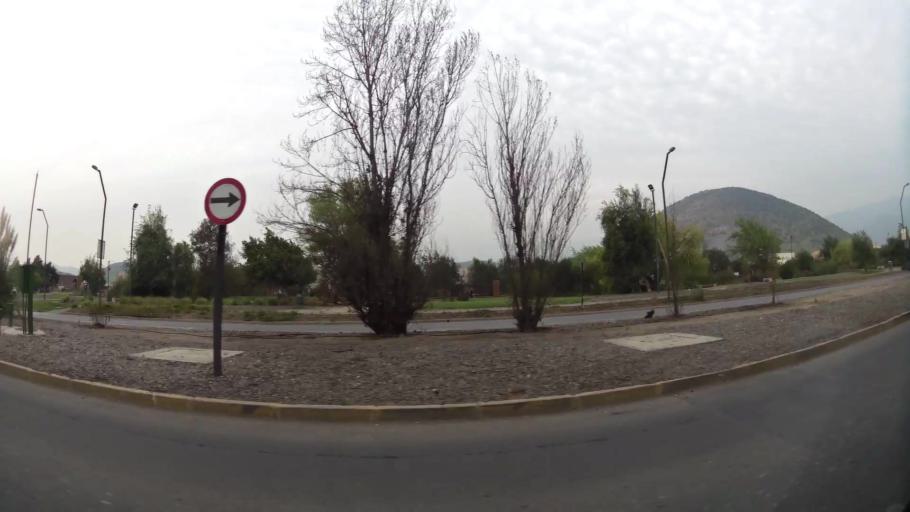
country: CL
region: Santiago Metropolitan
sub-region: Provincia de Chacabuco
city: Chicureo Abajo
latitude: -33.3073
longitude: -70.6627
